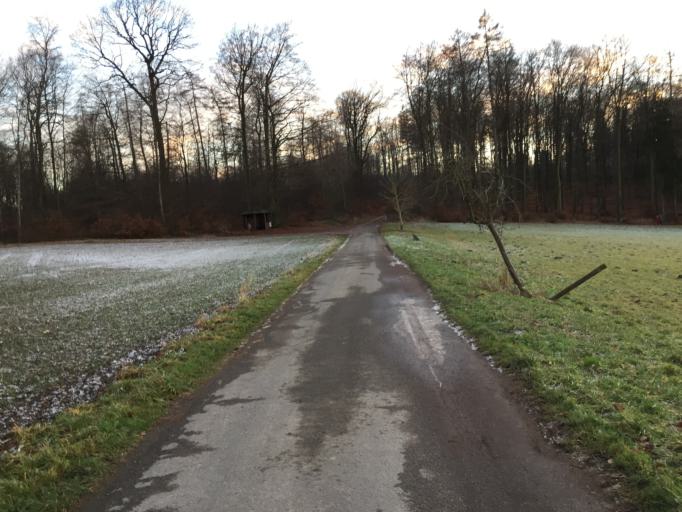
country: DE
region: Rheinland-Pfalz
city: Hardert
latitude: 50.5108
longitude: 7.5222
